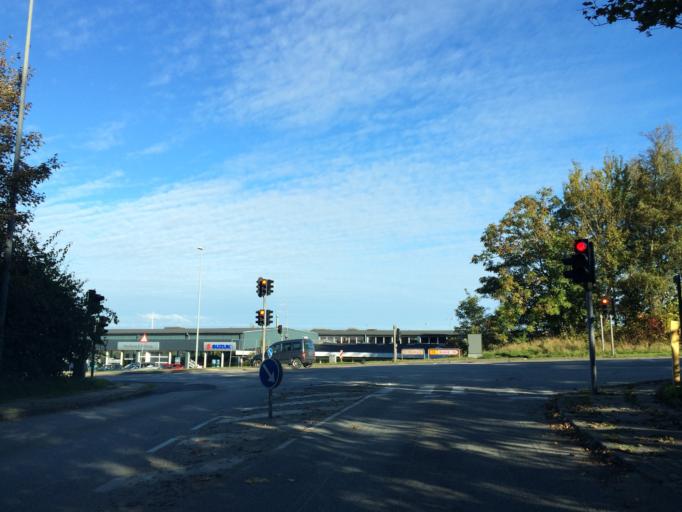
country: DK
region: Central Jutland
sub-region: Randers Kommune
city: Randers
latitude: 56.4470
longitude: 10.0658
